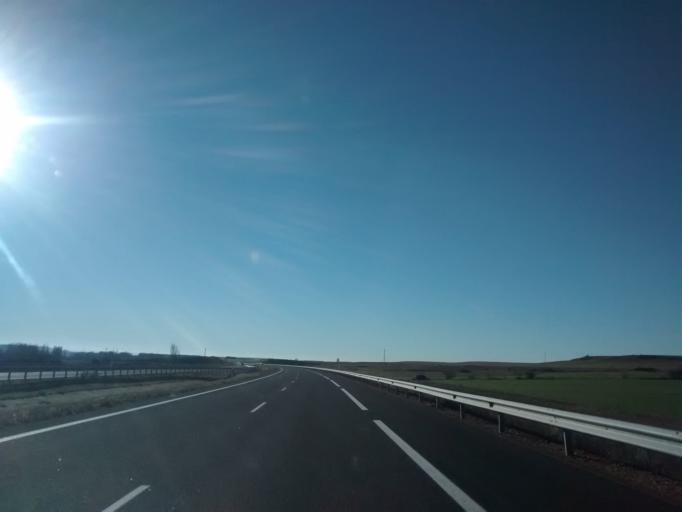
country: ES
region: Castille and Leon
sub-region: Provincia de Palencia
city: Espinosa de Villagonzalo
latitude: 42.4803
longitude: -4.3865
